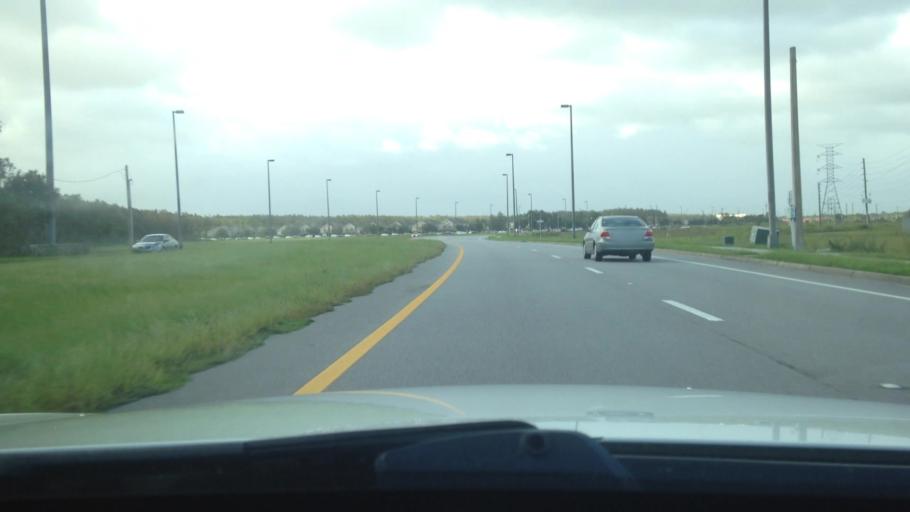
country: US
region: Florida
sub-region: Orange County
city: Conway
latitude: 28.4620
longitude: -81.2877
